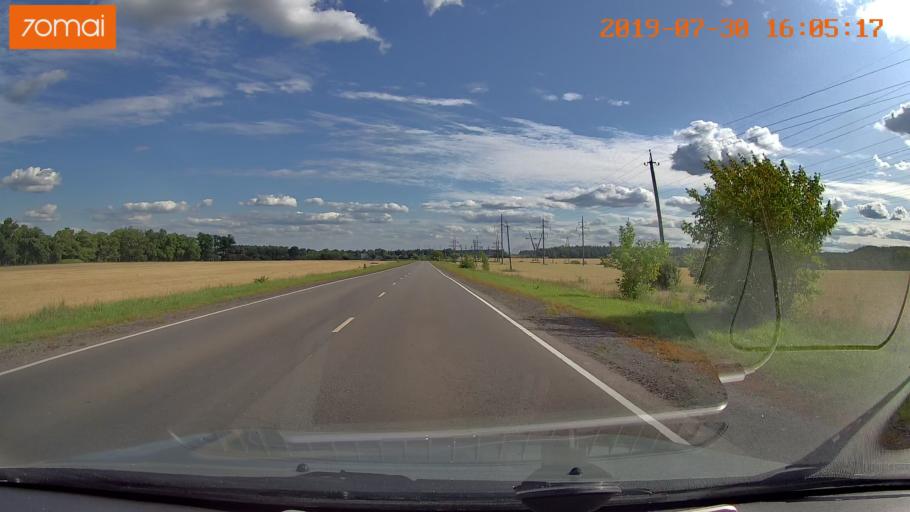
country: RU
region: Moskovskaya
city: Peski
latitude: 55.2678
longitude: 38.7145
